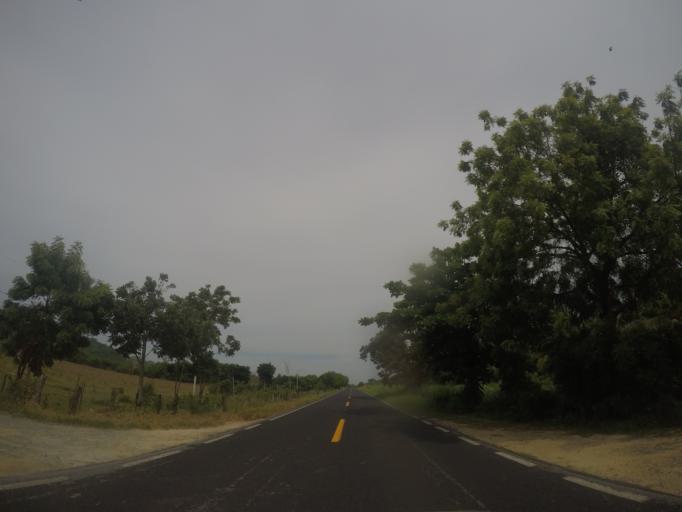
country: MX
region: Oaxaca
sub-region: Villa de Tututepec de Melchor Ocampo
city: Santa Rosa de Lima
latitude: 16.0241
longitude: -97.5573
